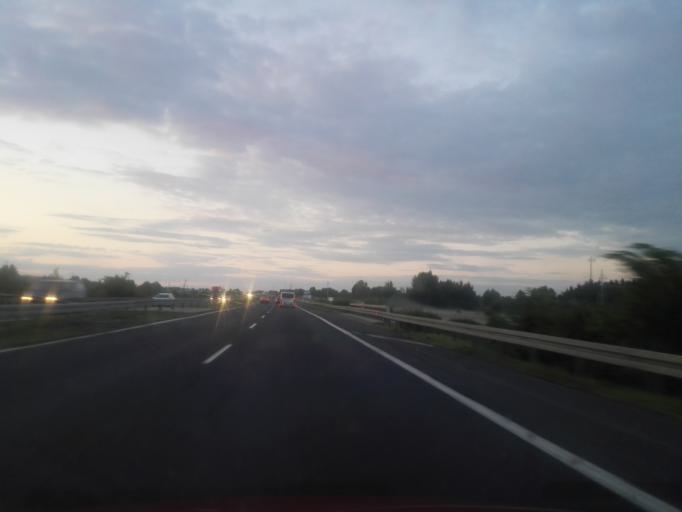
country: PL
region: Lodz Voivodeship
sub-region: Powiat radomszczanski
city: Gomunice
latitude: 51.1745
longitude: 19.4655
